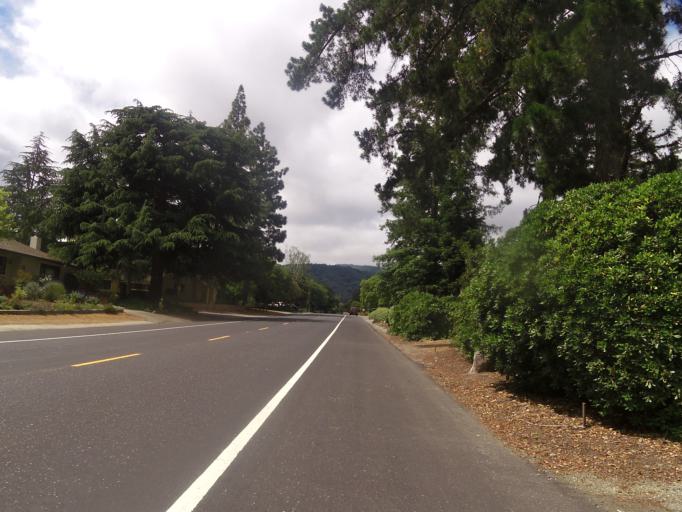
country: US
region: California
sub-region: Santa Clara County
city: Loyola
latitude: 37.3473
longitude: -122.0820
